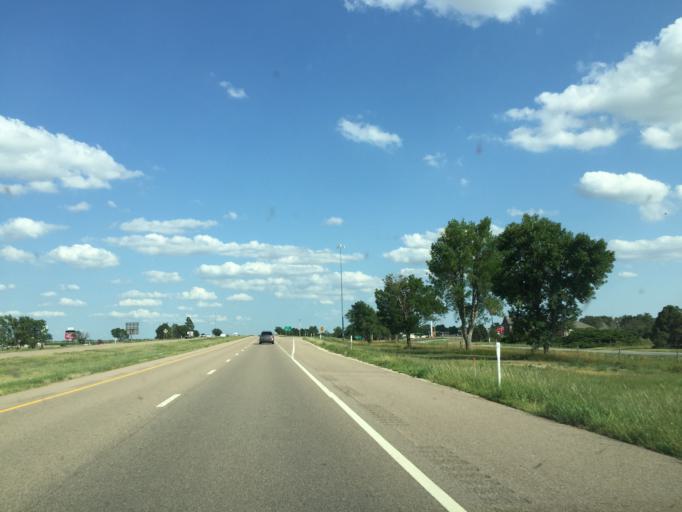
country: US
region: Kansas
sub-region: Gove County
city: Gove
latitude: 39.0597
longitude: -100.2456
